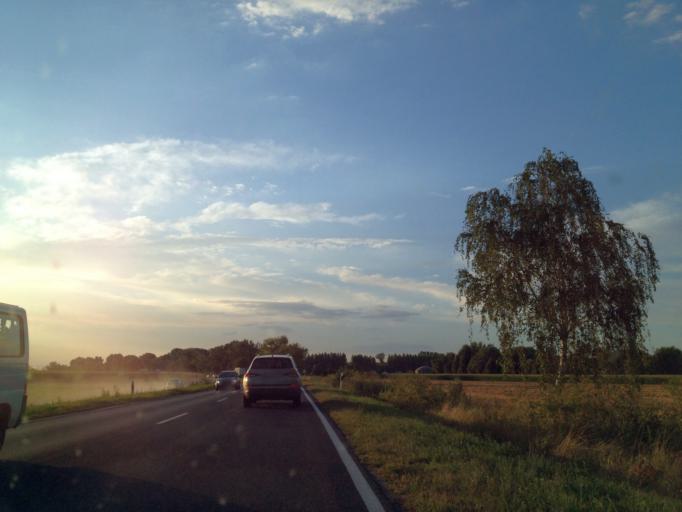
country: HU
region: Gyor-Moson-Sopron
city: Mosonmagyarovar
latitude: 47.8355
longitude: 17.2961
